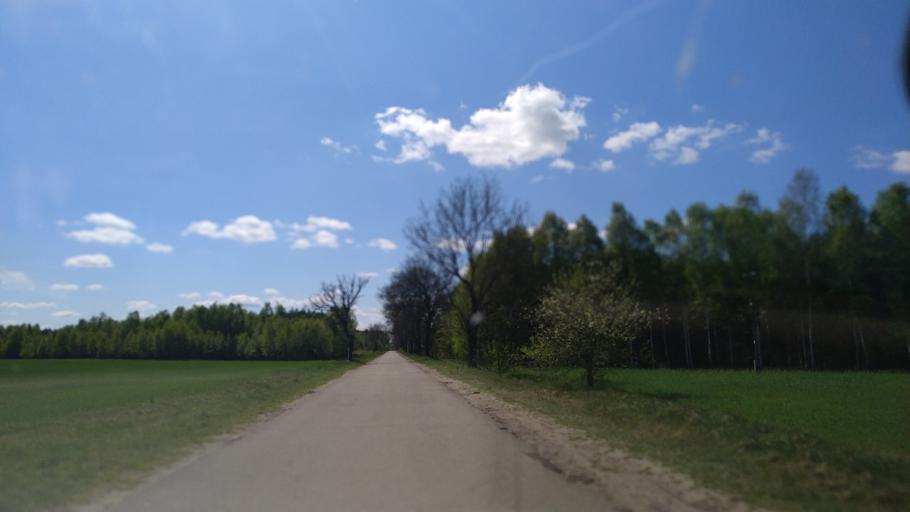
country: PL
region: Greater Poland Voivodeship
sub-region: Powiat zlotowski
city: Tarnowka
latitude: 53.2698
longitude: 16.7995
